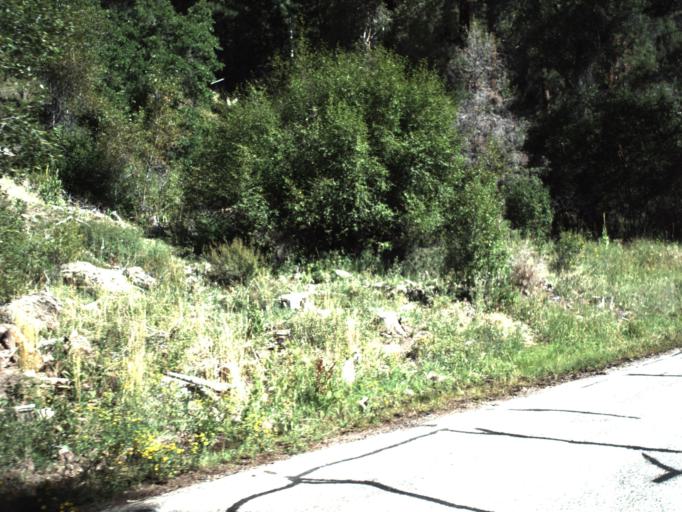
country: US
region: Utah
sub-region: Beaver County
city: Beaver
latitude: 38.2662
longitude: -112.4892
